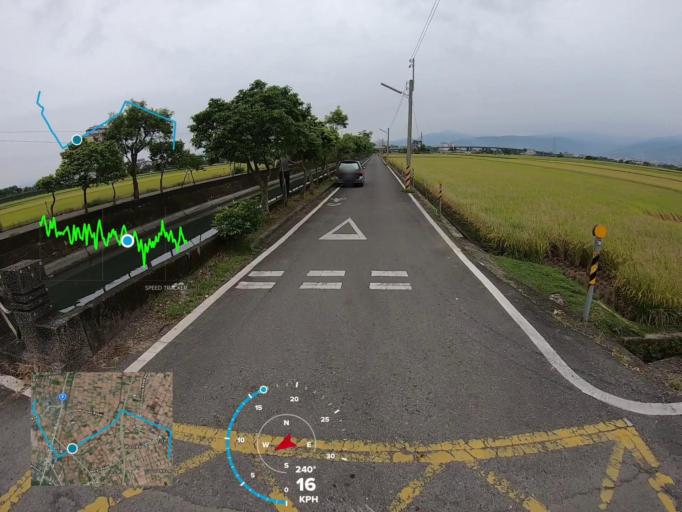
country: TW
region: Taiwan
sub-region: Yilan
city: Yilan
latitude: 24.7776
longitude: 121.7683
